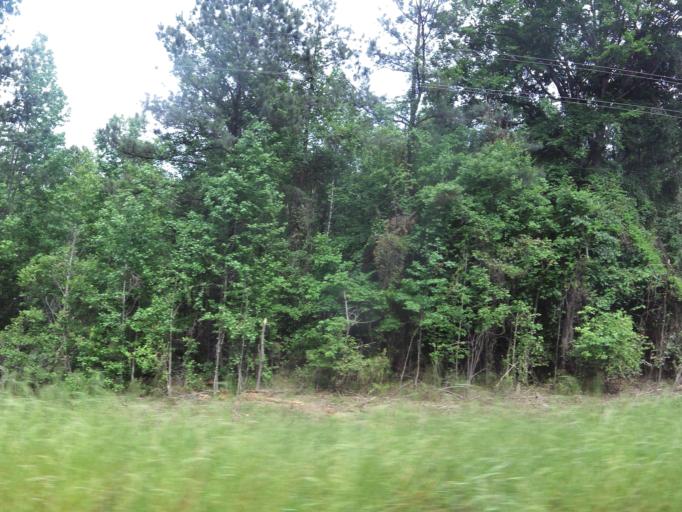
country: US
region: Georgia
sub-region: Jefferson County
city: Wrens
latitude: 33.3336
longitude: -82.4556
